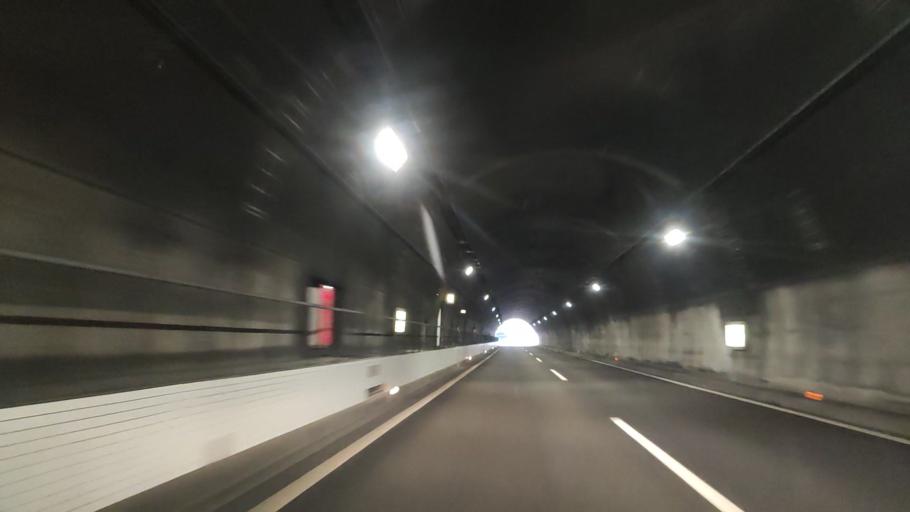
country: JP
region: Ehime
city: Saijo
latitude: 33.8480
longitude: 132.9956
